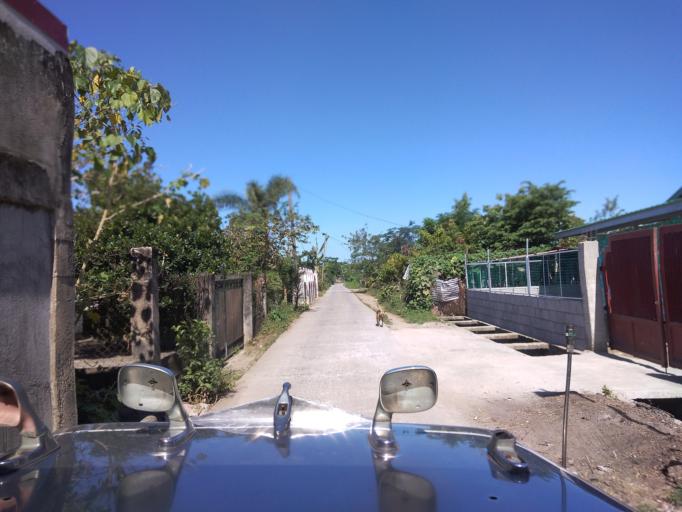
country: PH
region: Central Luzon
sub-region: Province of Pampanga
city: Salapungan
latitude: 15.1543
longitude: 120.9210
